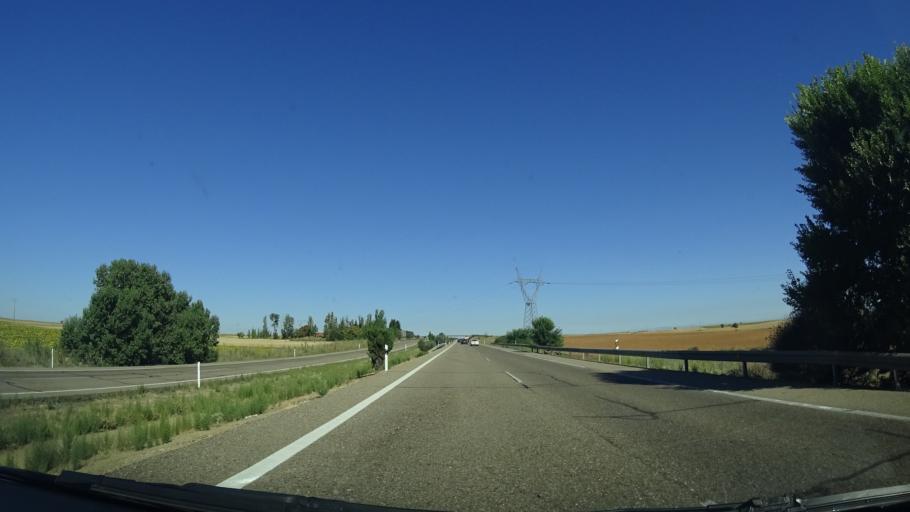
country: ES
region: Castille and Leon
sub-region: Provincia de Zamora
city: Cerecinos de Campos
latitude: 41.9164
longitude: -5.5126
